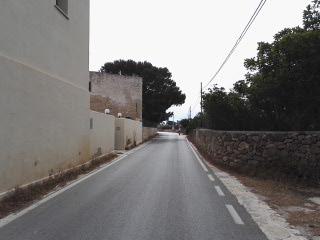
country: IT
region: Sicily
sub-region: Trapani
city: Favignana
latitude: 37.9232
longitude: 12.3382
